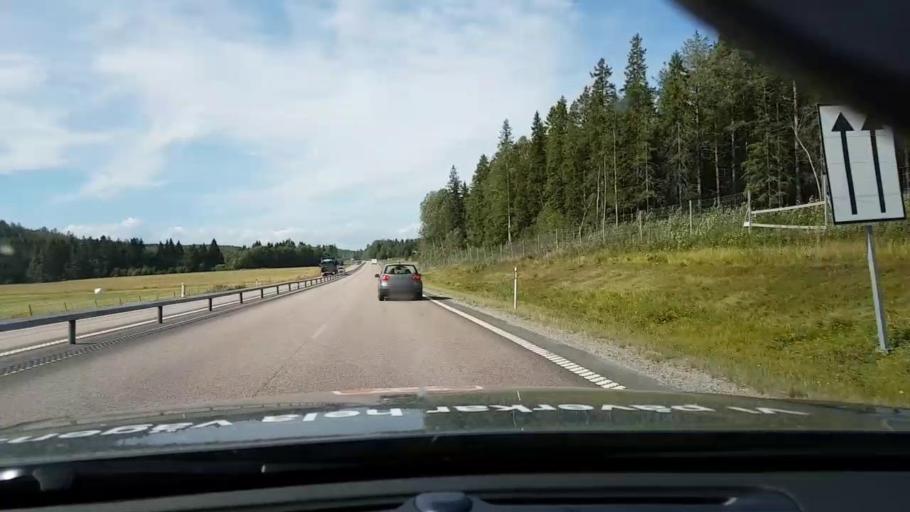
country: SE
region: Vaesternorrland
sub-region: OErnskoeldsviks Kommun
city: Ornskoldsvik
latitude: 63.2988
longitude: 18.8672
